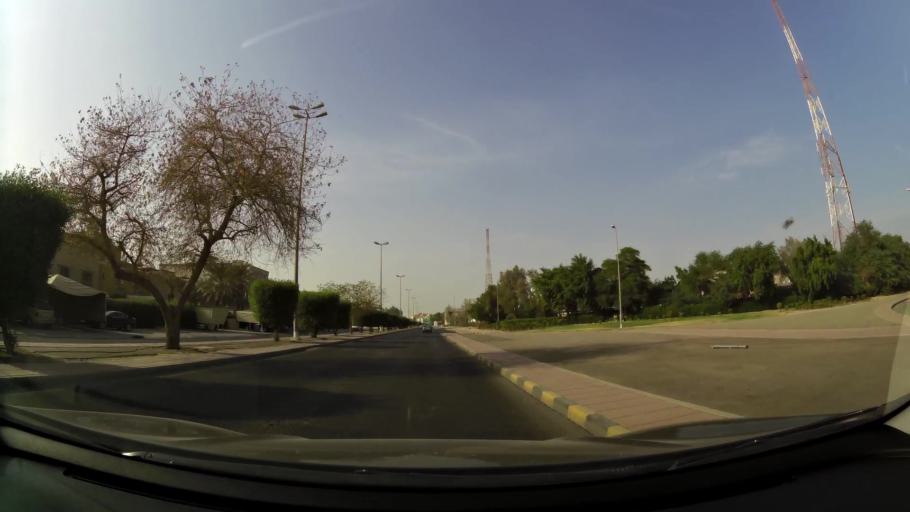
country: KW
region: Mubarak al Kabir
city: Mubarak al Kabir
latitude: 29.1689
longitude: 48.0794
